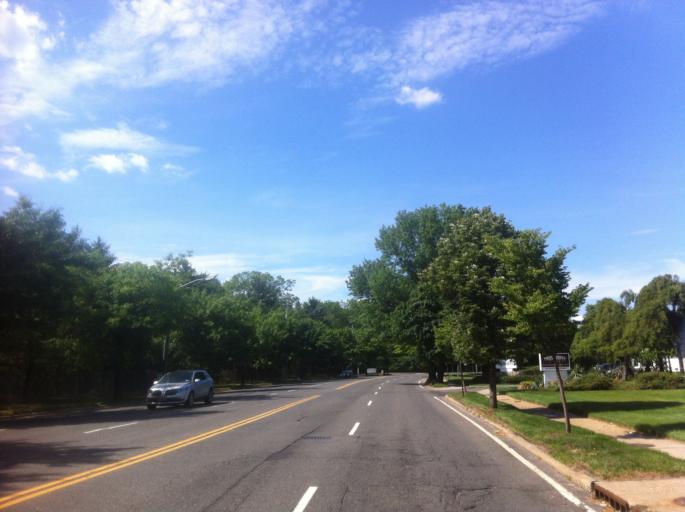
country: US
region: New York
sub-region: Nassau County
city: Syosset
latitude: 40.8108
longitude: -73.5142
